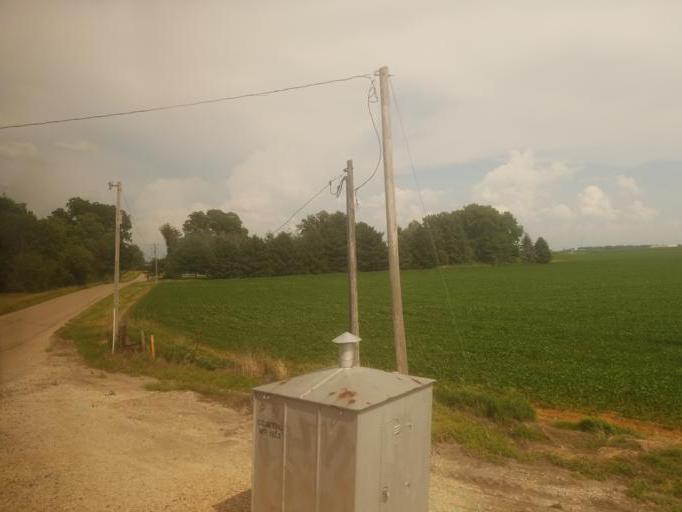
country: US
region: Illinois
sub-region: Knox County
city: Galesburg
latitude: 40.9183
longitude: -90.4108
